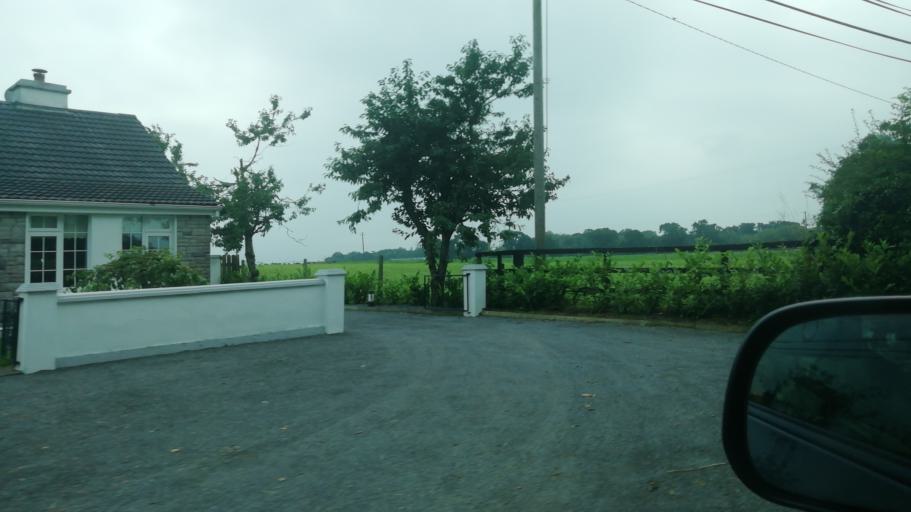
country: IE
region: Munster
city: Fethard
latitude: 52.5431
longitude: -7.6815
